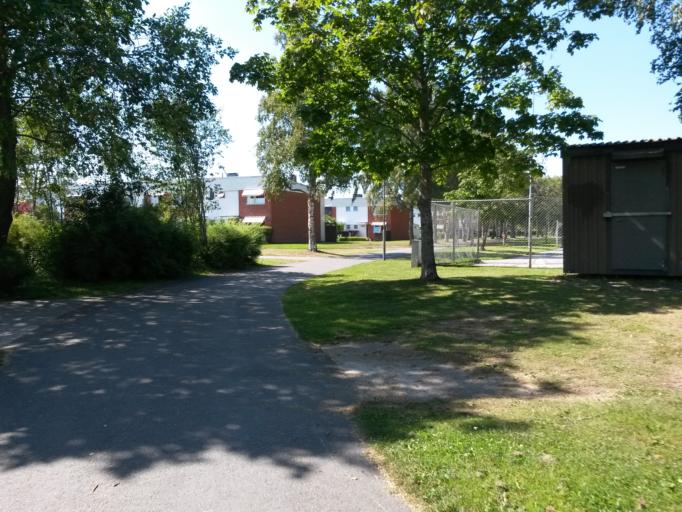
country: SE
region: Vaestra Goetaland
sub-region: Lidkopings Kommun
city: Lidkoping
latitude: 58.4873
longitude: 13.1466
